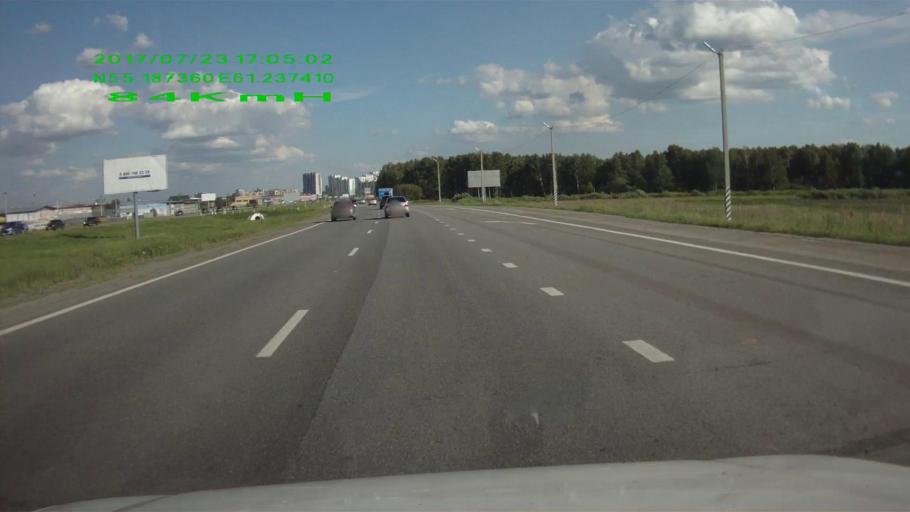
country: RU
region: Chelyabinsk
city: Roshchino
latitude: 55.1867
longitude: 61.2387
